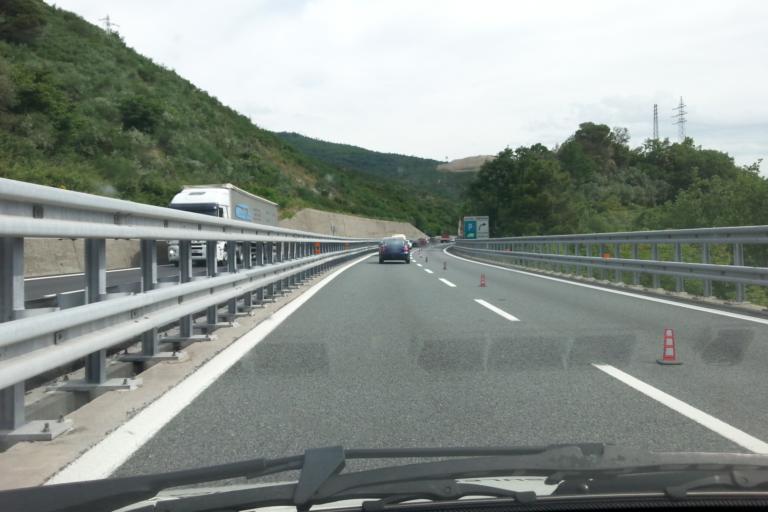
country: IT
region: Liguria
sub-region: Provincia di Savona
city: Valle di Vado
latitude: 44.2587
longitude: 8.4069
